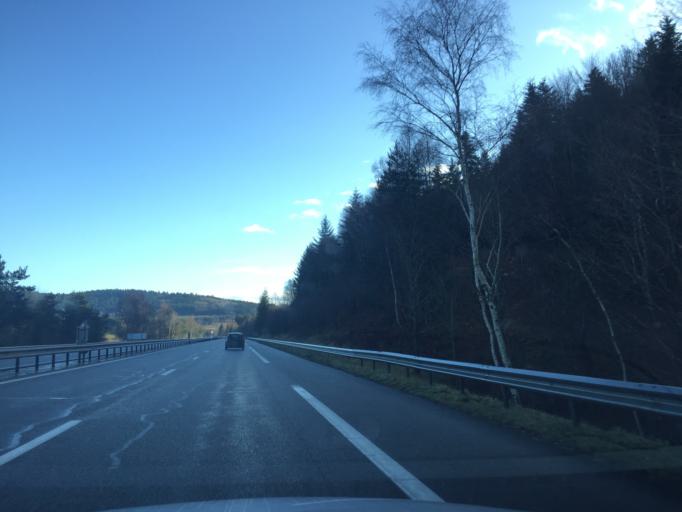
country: FR
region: Rhone-Alpes
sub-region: Departement de la Loire
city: Noiretable
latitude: 45.8491
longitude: 3.7312
